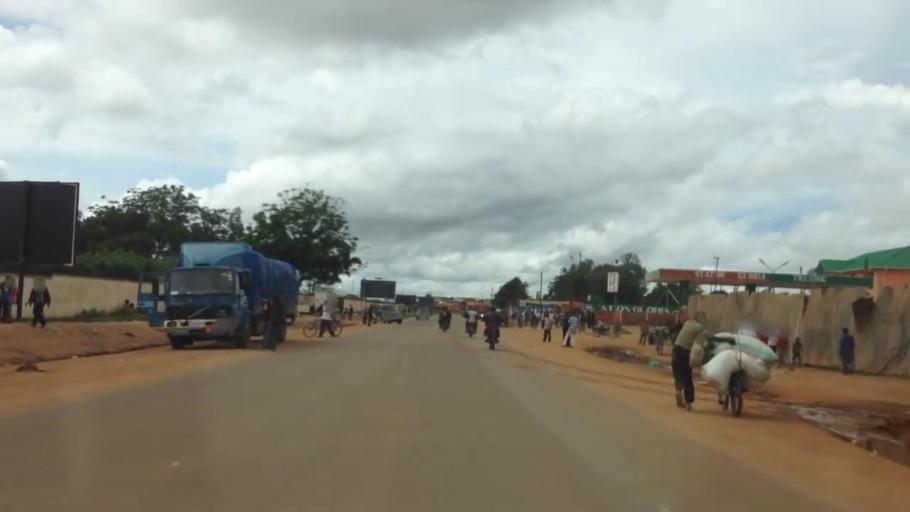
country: CD
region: Katanga
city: Kolwezi
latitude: -10.7207
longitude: 25.5060
